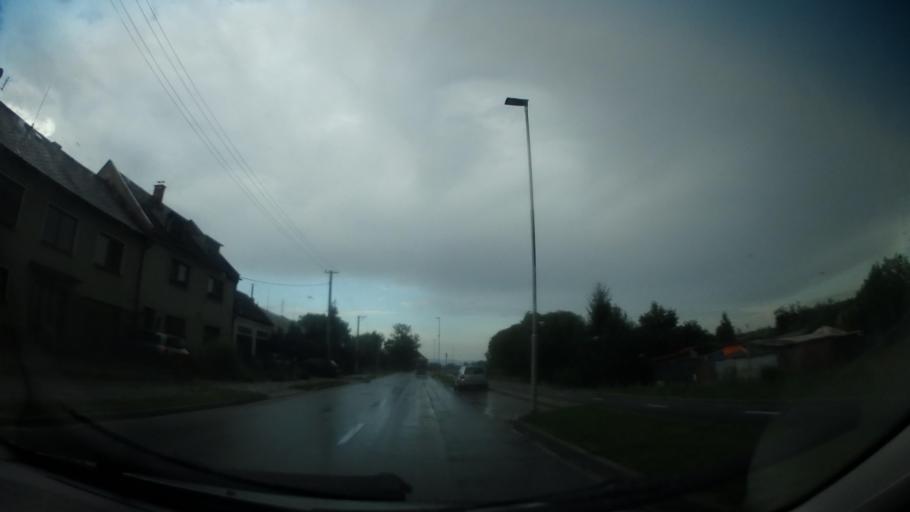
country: CZ
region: Olomoucky
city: Litovel
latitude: 49.7081
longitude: 17.0832
